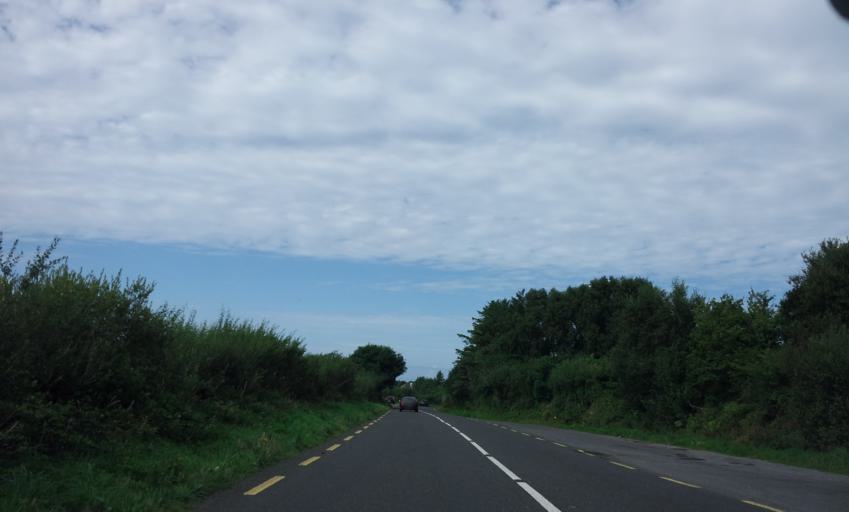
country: IE
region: Munster
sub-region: Ciarrai
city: Killorglin
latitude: 52.0701
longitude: -9.8888
